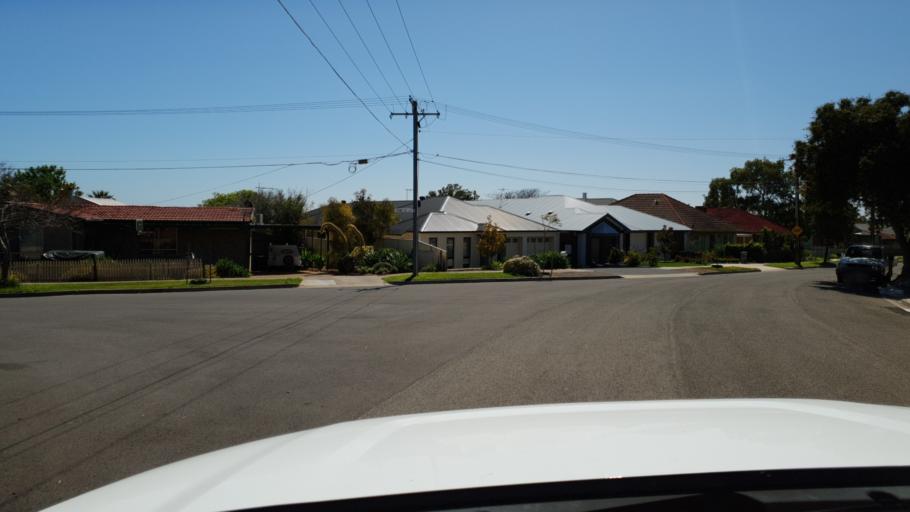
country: AU
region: South Australia
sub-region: Holdfast Bay
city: Seacliff Park
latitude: -35.0289
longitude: 138.5299
